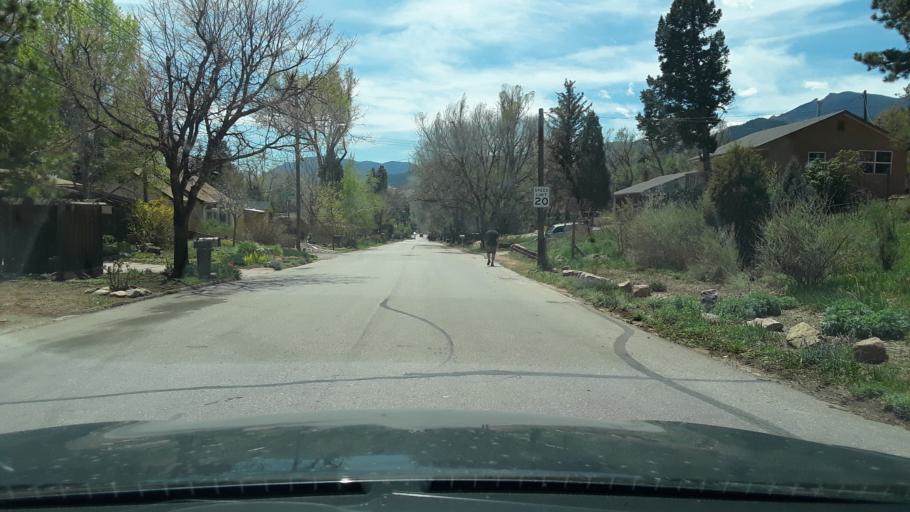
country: US
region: Colorado
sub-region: El Paso County
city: Manitou Springs
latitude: 38.8650
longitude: -104.8848
